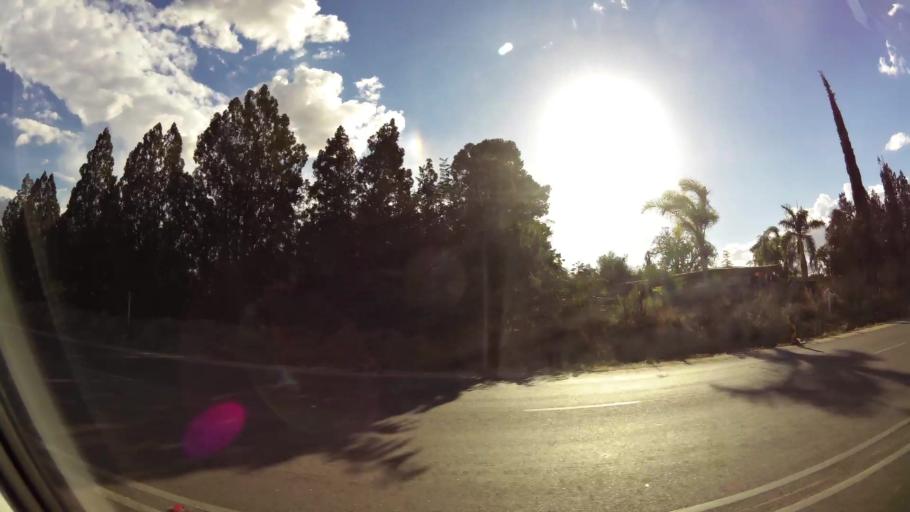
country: ZA
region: Limpopo
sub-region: Capricorn District Municipality
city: Polokwane
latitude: -23.9401
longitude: 29.4486
